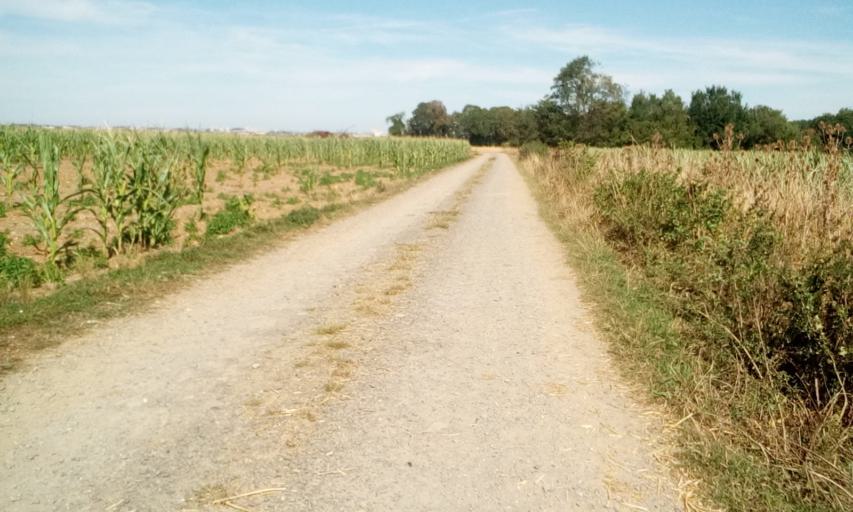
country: FR
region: Lower Normandy
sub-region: Departement du Calvados
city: Fontaine-Etoupefour
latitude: 49.1406
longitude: -0.4415
